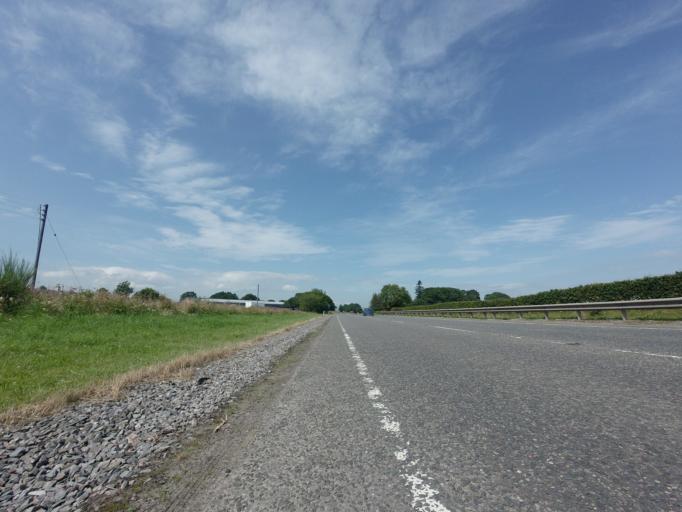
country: GB
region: Scotland
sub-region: Highland
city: Tain
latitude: 57.8216
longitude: -4.0756
